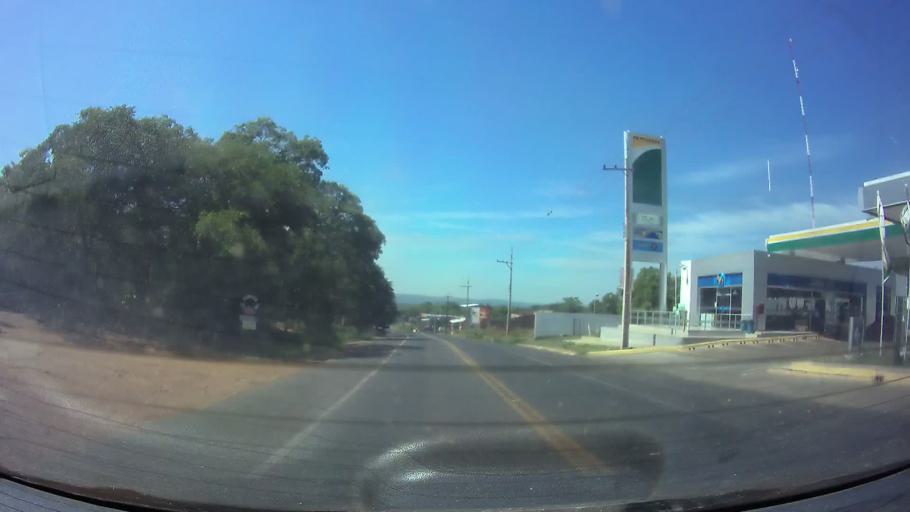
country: PY
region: Central
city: Aregua
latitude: -25.2386
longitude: -57.4321
